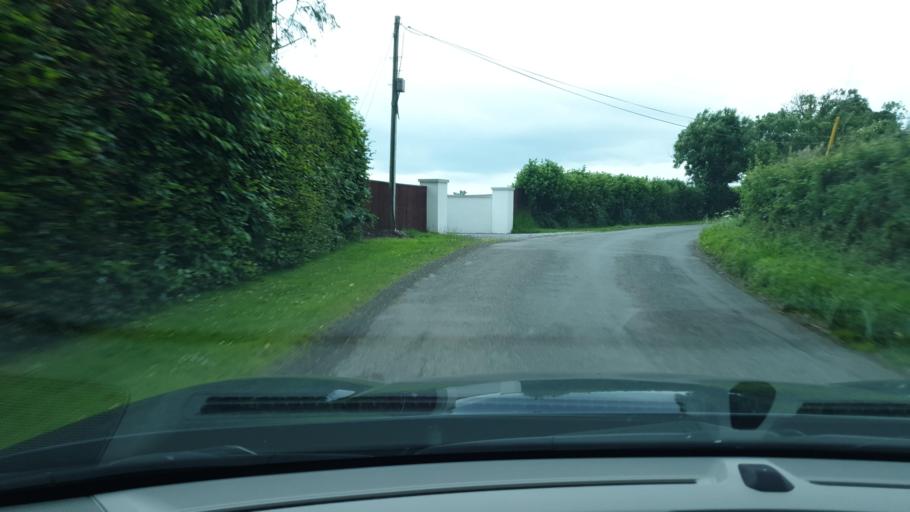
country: IE
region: Leinster
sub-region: An Mhi
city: Navan
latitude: 53.5912
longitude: -6.6262
